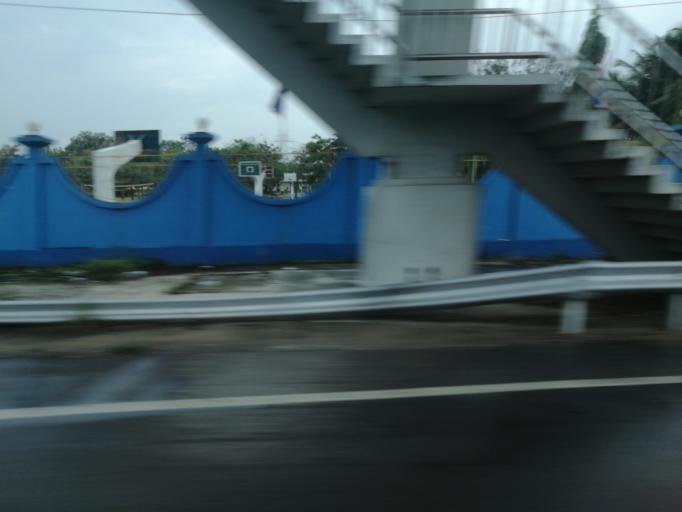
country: TH
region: Prachuap Khiri Khan
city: Kui Buri
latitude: 12.0816
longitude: 99.8561
